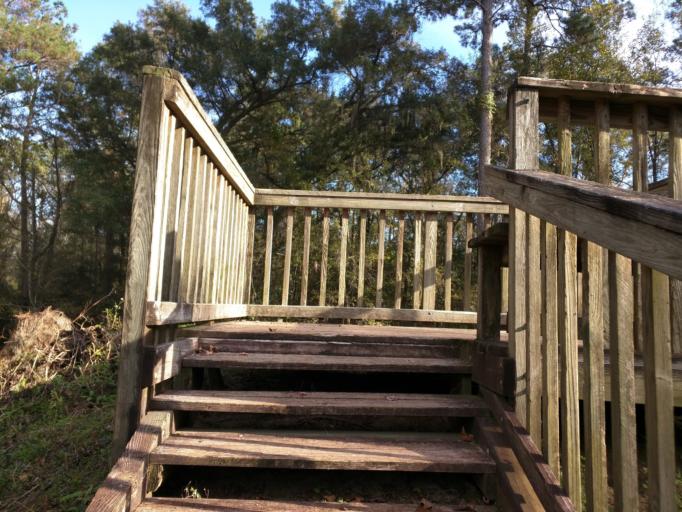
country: US
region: Florida
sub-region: Leon County
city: Tallahassee
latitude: 30.5008
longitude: -84.3136
